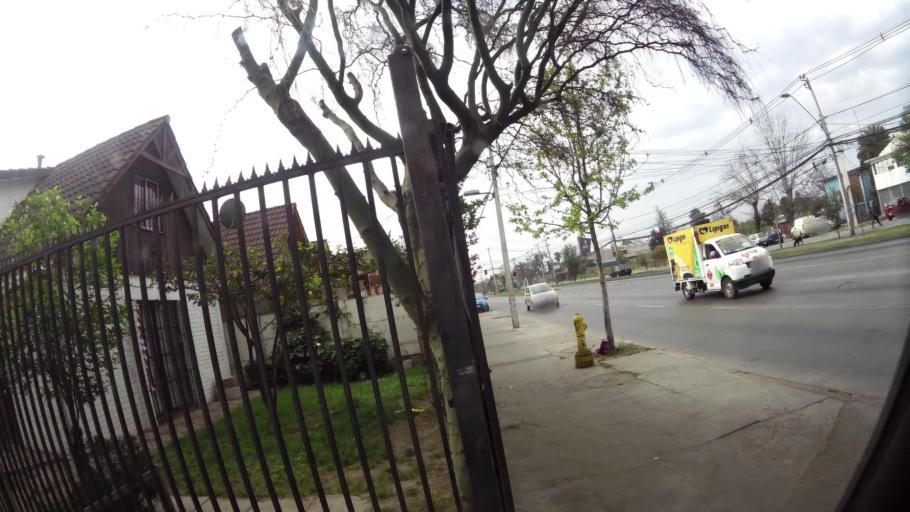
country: CL
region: Santiago Metropolitan
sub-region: Provincia de Santiago
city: Lo Prado
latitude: -33.5218
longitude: -70.7574
